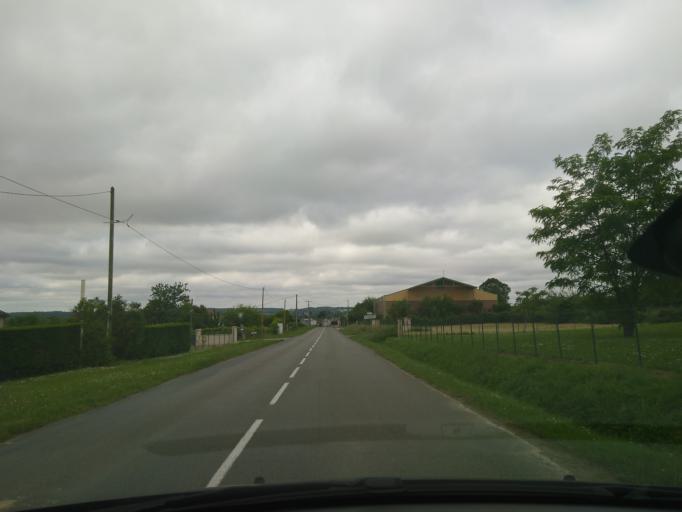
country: FR
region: Aquitaine
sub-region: Departement du Lot-et-Garonne
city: Cancon
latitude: 44.5387
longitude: 0.6160
